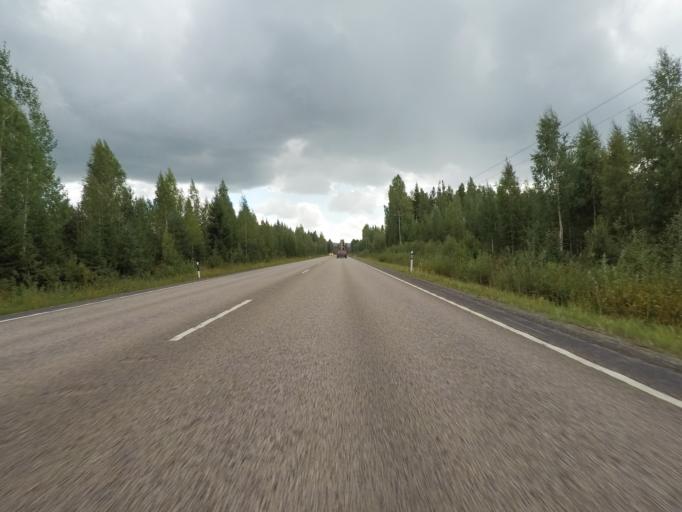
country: FI
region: Central Finland
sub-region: Joutsa
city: Leivonmaeki
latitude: 61.9425
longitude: 26.1114
